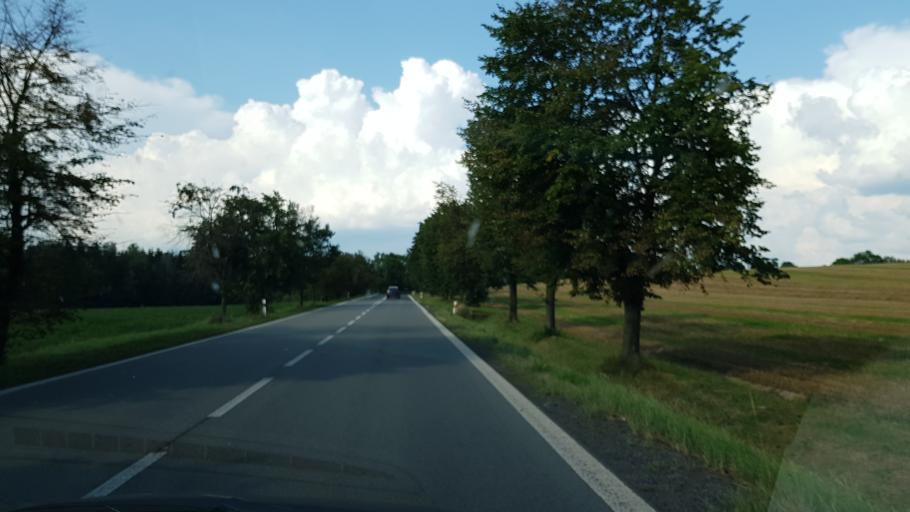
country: CZ
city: Vamberk
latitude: 50.1092
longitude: 16.3793
